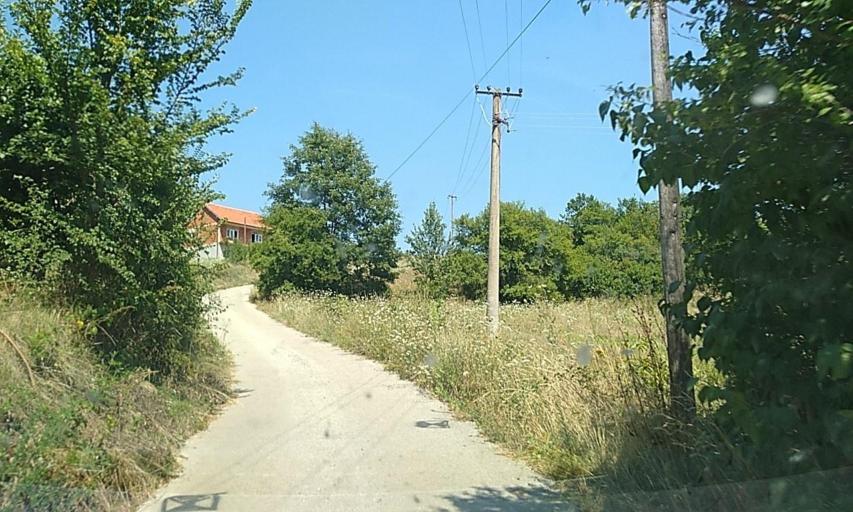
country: RS
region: Central Serbia
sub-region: Pcinjski Okrug
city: Vladicin Han
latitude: 42.7570
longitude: 22.0745
